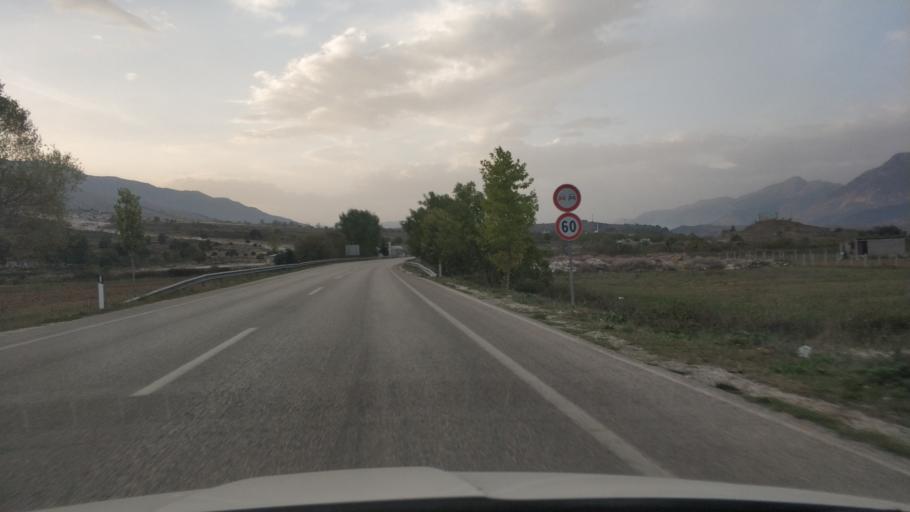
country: AL
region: Gjirokaster
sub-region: Rrethi i Gjirokastres
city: Dervician
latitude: 40.0377
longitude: 20.1782
